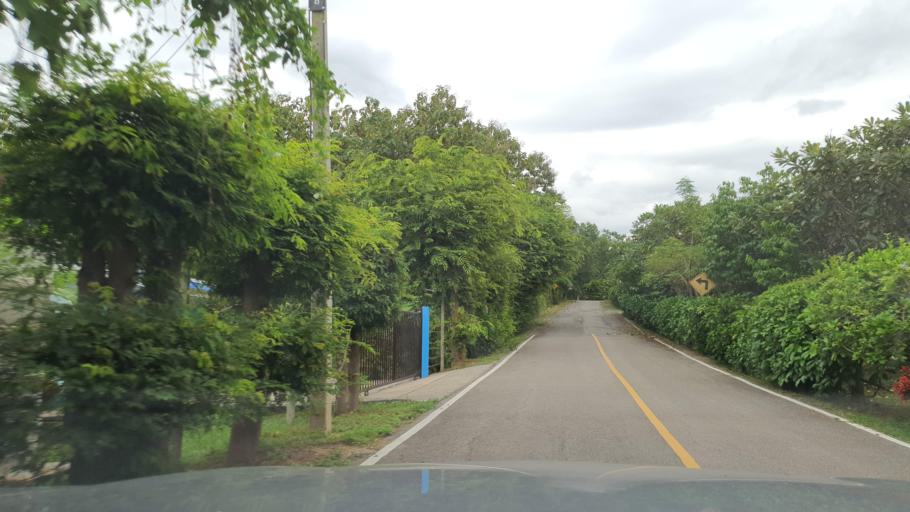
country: TH
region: Chiang Mai
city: Chiang Mai
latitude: 18.9299
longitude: 98.9053
